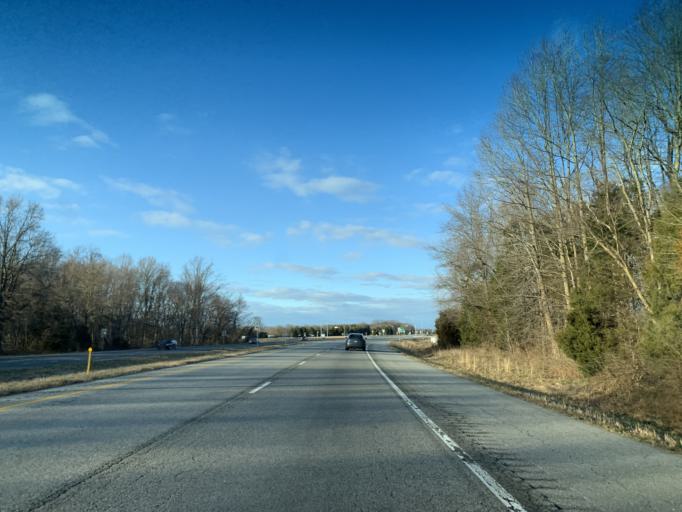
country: US
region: Maryland
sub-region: Queen Anne's County
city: Kingstown
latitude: 39.2389
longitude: -75.8751
